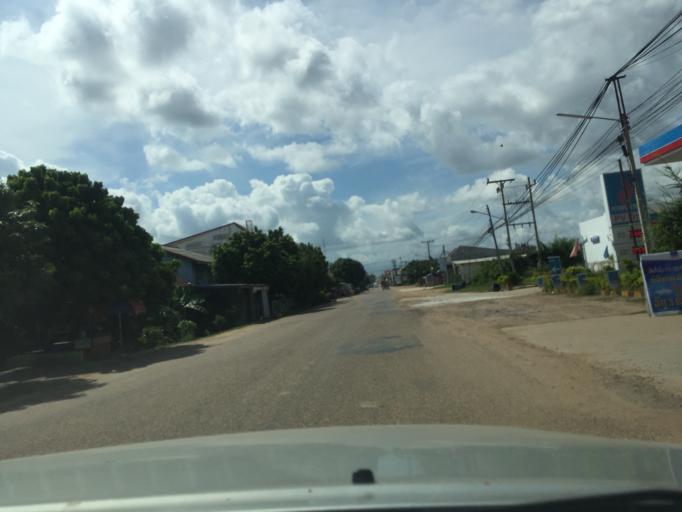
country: LA
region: Savannahkhet
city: Savannakhet
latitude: 16.5501
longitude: 104.7485
